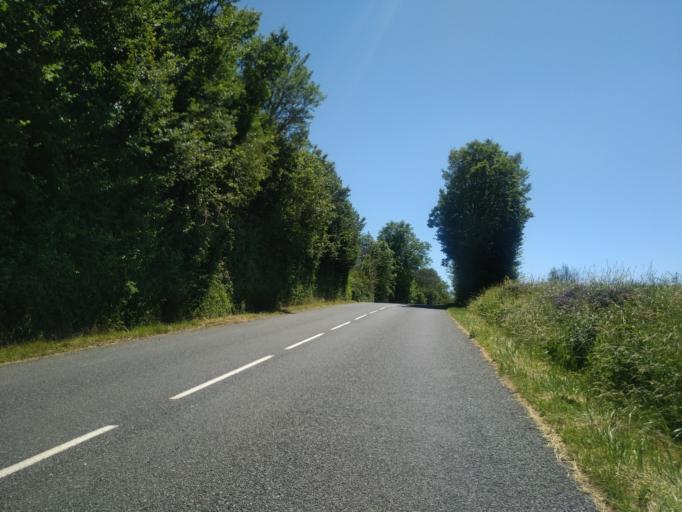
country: FR
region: Rhone-Alpes
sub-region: Departement du Rhone
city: Limonest
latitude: 45.8433
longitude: 4.7932
